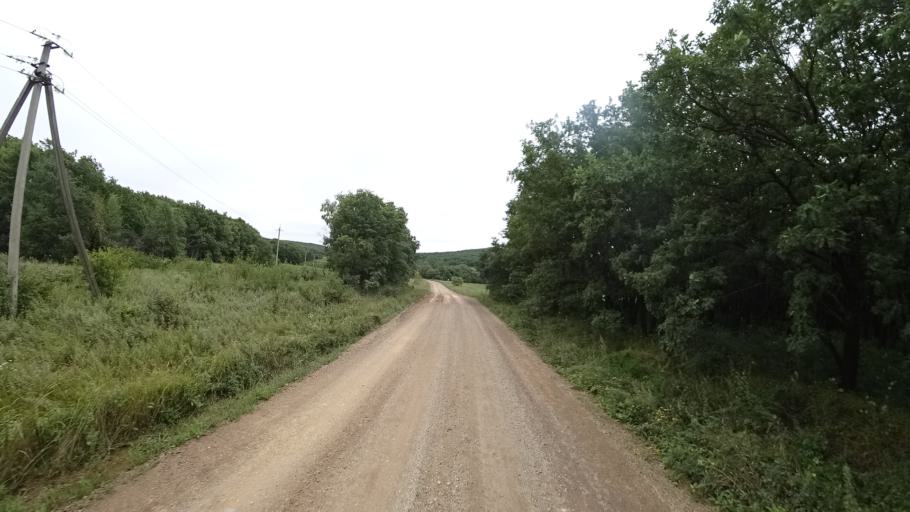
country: RU
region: Primorskiy
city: Lyalichi
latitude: 44.0589
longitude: 132.4771
